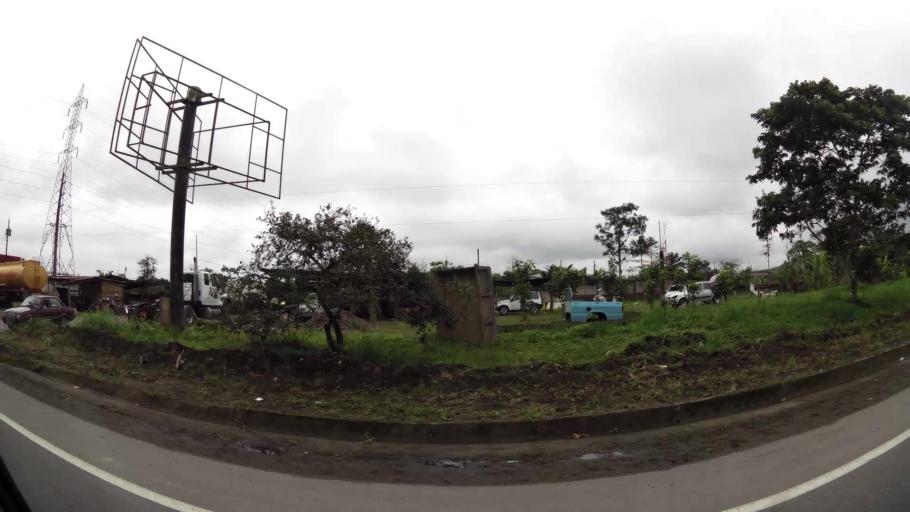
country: EC
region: Santo Domingo de los Tsachilas
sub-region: Canton Santo Domingo de los Colorados
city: Santo Domingo de los Colorados
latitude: -0.2600
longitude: -79.1251
